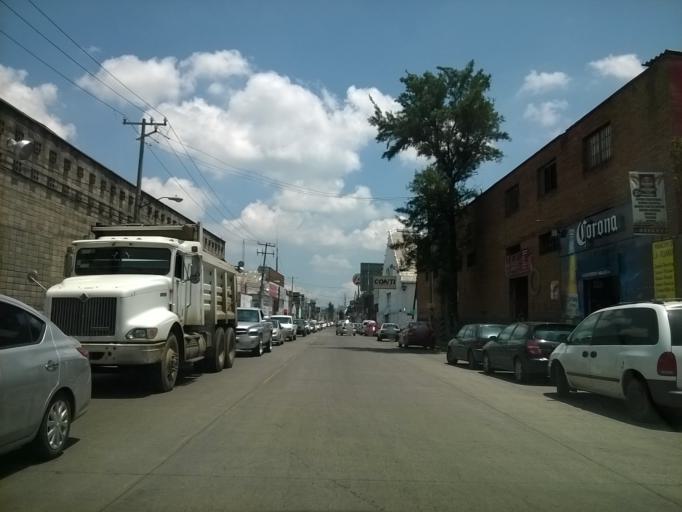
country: MX
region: Michoacan
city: Morelia
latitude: 19.7073
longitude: -101.1979
